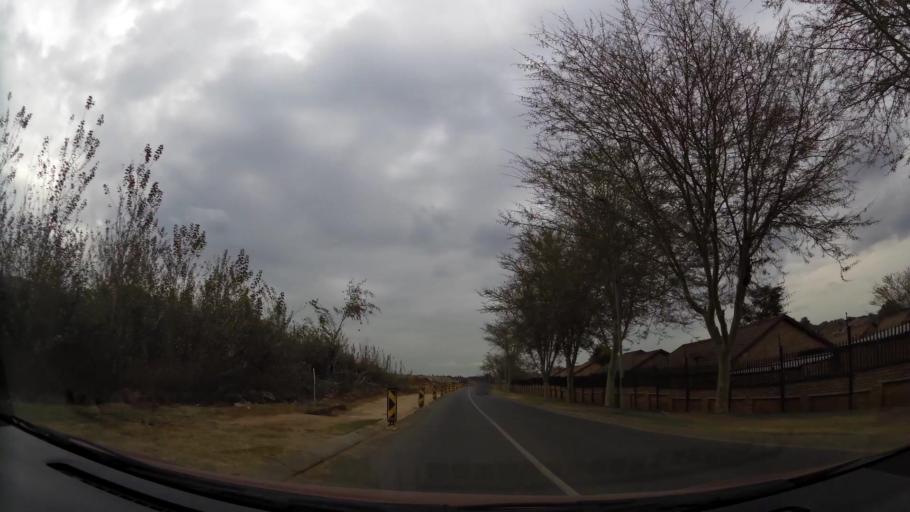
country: ZA
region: Gauteng
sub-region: City of Johannesburg Metropolitan Municipality
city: Roodepoort
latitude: -26.1112
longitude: 27.8919
